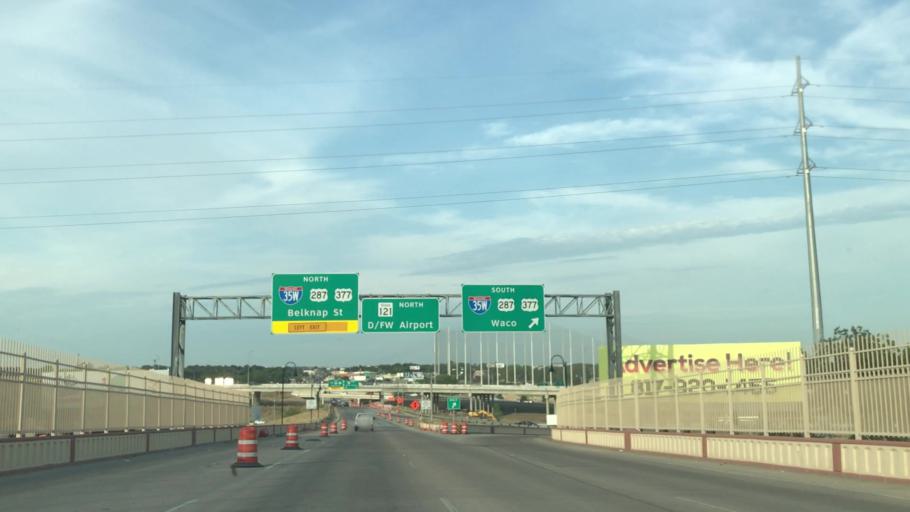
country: US
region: Texas
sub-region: Tarrant County
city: Fort Worth
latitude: 32.7627
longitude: -97.3215
